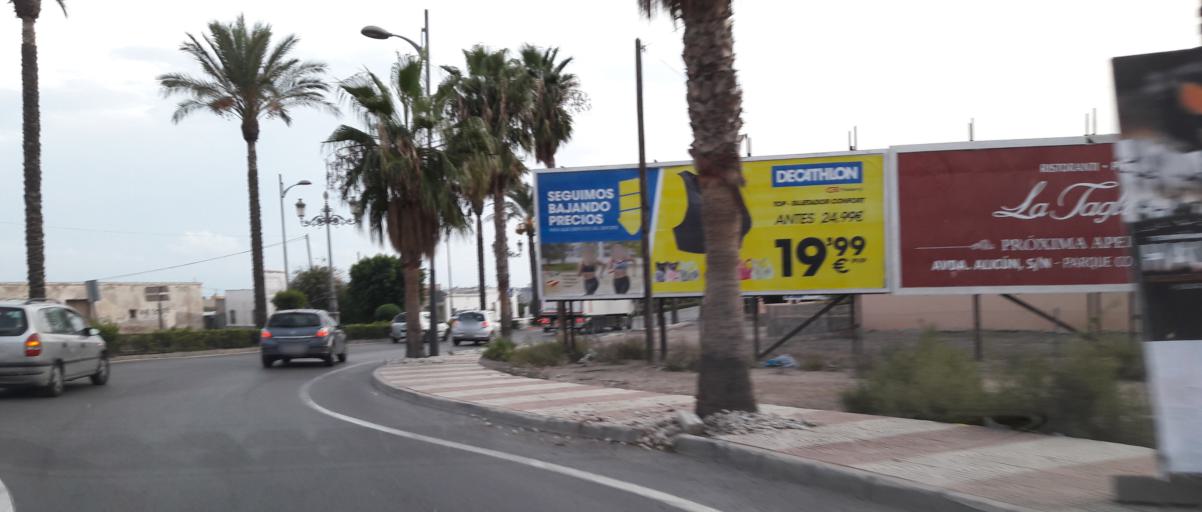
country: ES
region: Andalusia
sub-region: Provincia de Almeria
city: Roquetas de Mar
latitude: 36.7923
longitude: -2.6046
